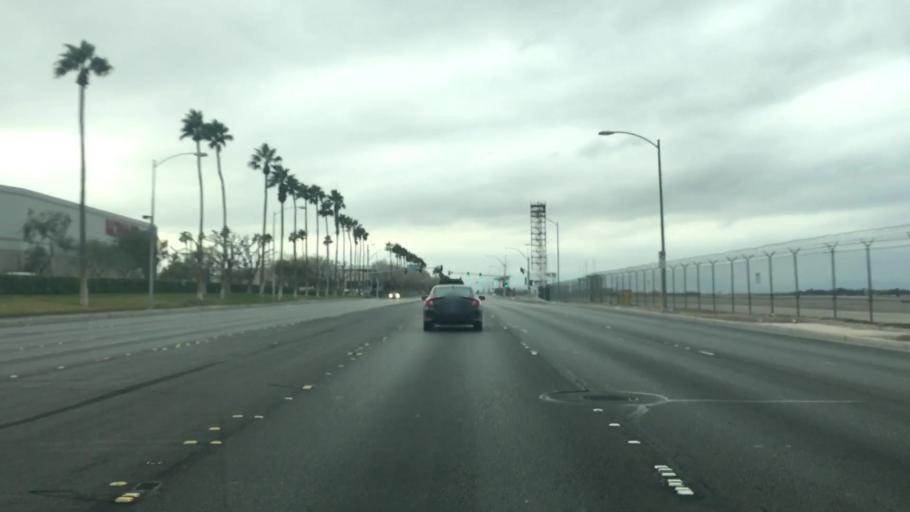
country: US
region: Nevada
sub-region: Clark County
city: Paradise
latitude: 36.0715
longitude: -115.1521
